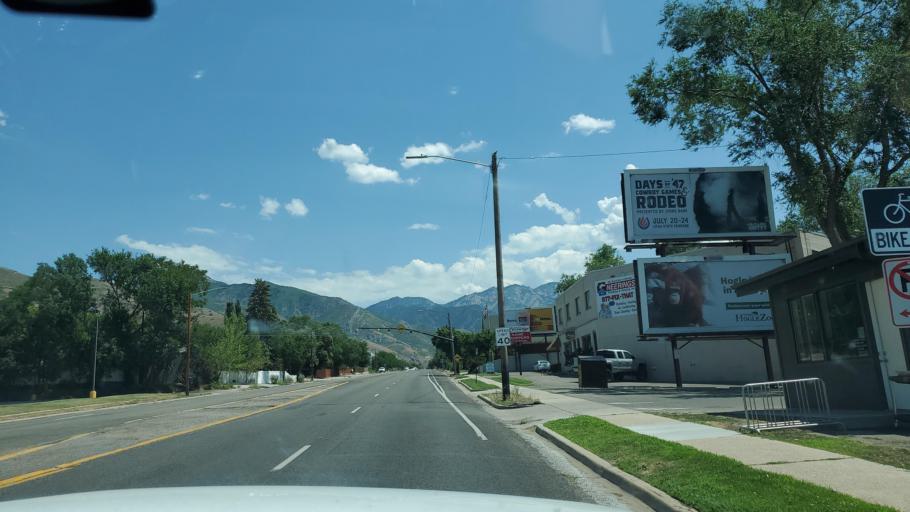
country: US
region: Utah
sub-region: Salt Lake County
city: Canyon Rim
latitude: 40.7247
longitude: -111.8238
